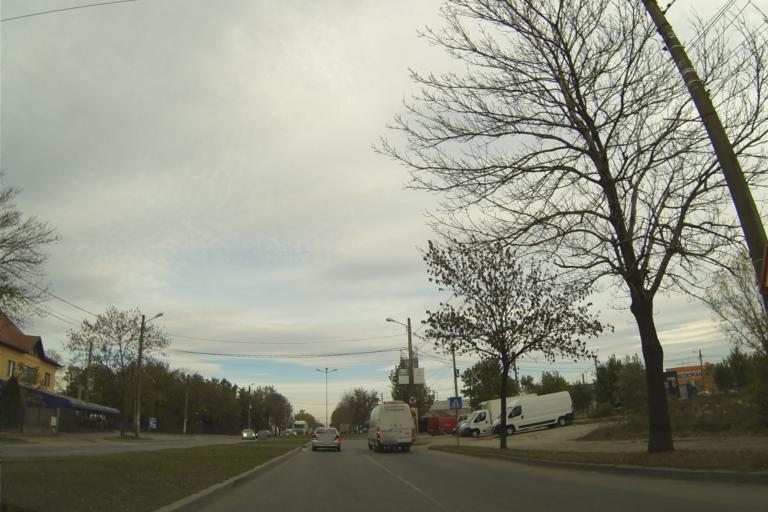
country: RO
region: Olt
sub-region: Municipiul Slatina
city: Slatina
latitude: 44.4416
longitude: 24.3753
